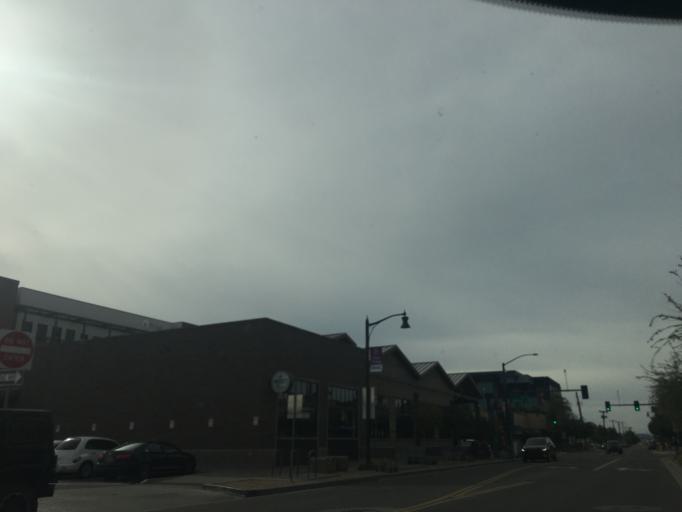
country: US
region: Arizona
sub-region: Maricopa County
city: Gilbert
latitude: 33.3562
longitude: -111.7887
